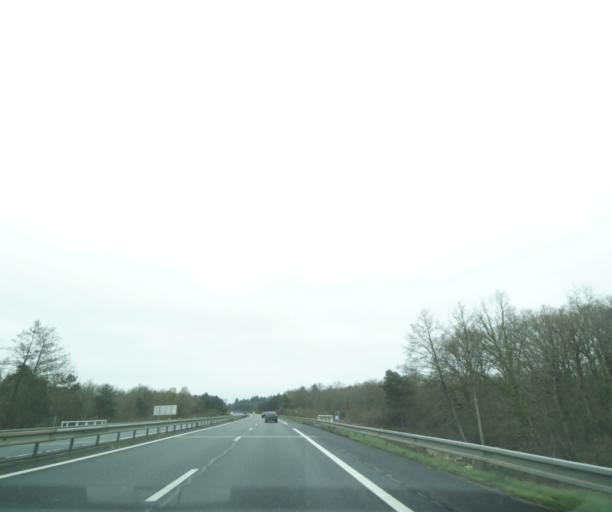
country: FR
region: Centre
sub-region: Departement du Loiret
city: La Ferte-Saint-Aubin
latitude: 47.6874
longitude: 1.9035
